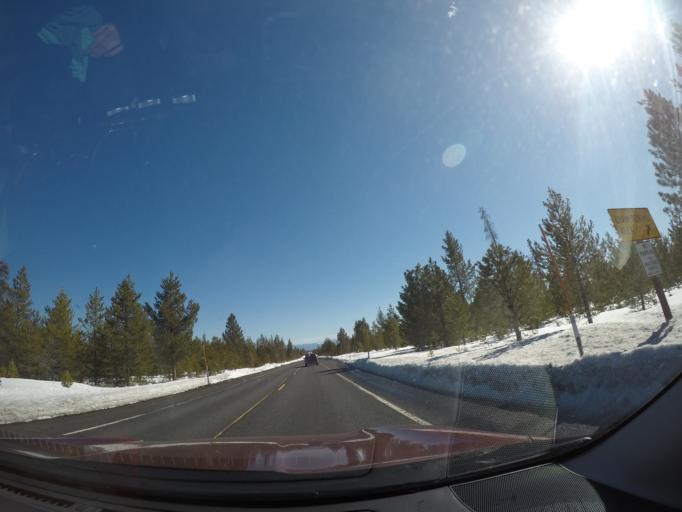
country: US
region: Oregon
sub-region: Deschutes County
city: Three Rivers
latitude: 43.8902
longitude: -121.5857
